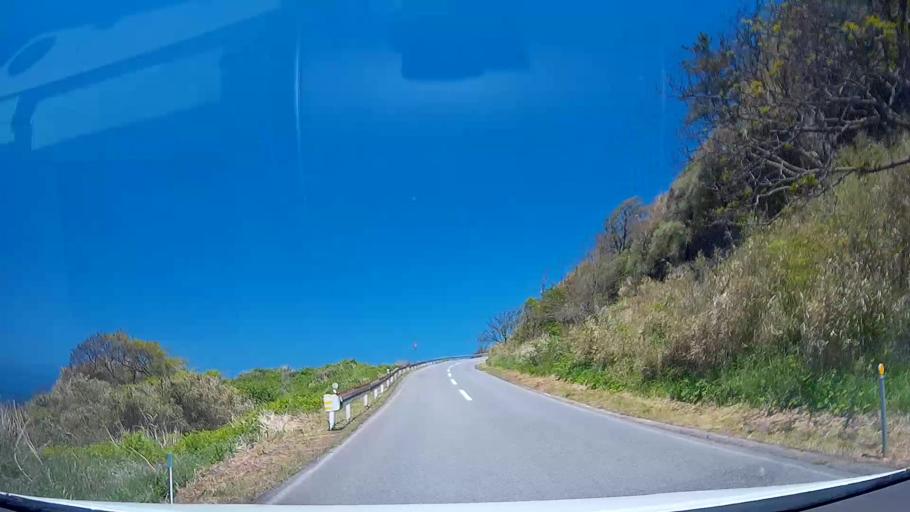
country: JP
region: Ishikawa
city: Nanao
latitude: 37.5228
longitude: 137.2475
